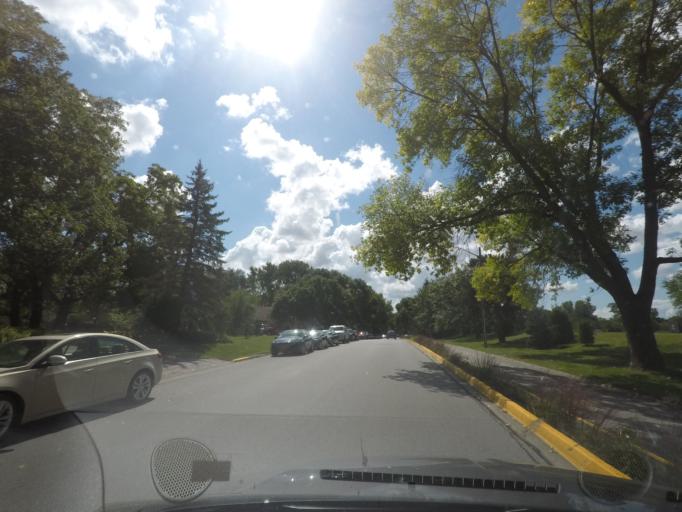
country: US
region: Iowa
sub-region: Story County
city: Ames
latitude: 42.0140
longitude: -93.6442
